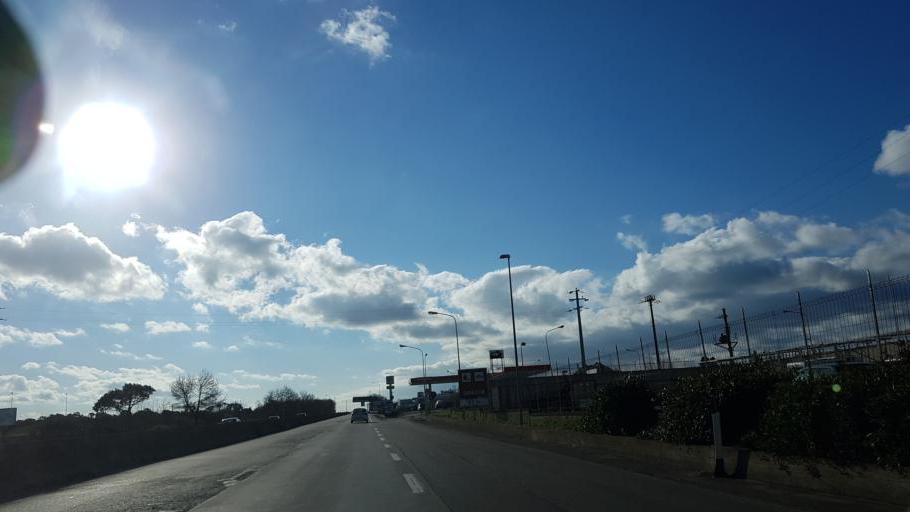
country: IT
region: Apulia
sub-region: Provincia di Brindisi
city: Brindisi
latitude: 40.6339
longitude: 17.9170
